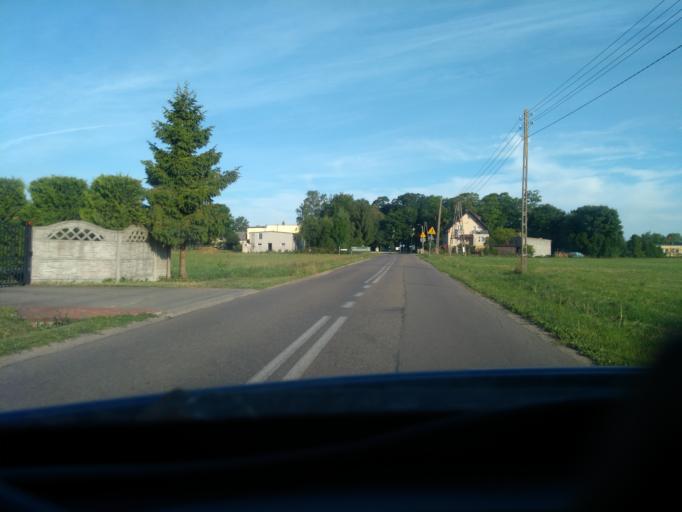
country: PL
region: Pomeranian Voivodeship
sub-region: Powiat kartuski
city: Przodkowo
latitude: 54.3988
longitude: 18.3339
